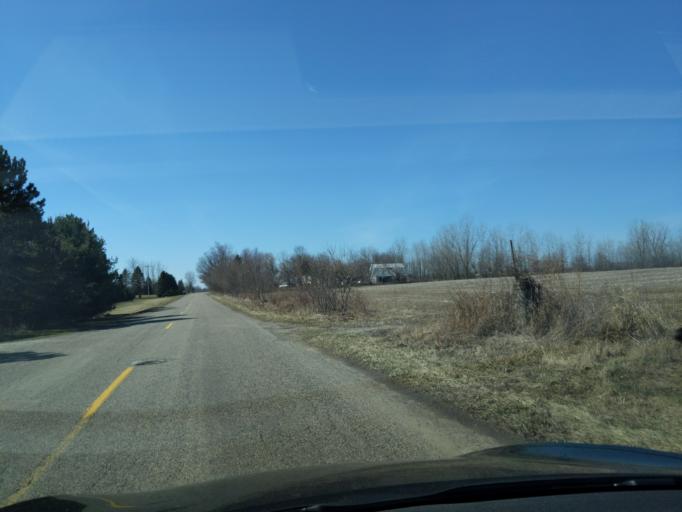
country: US
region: Michigan
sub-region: Ionia County
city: Portland
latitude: 42.7267
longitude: -84.9655
